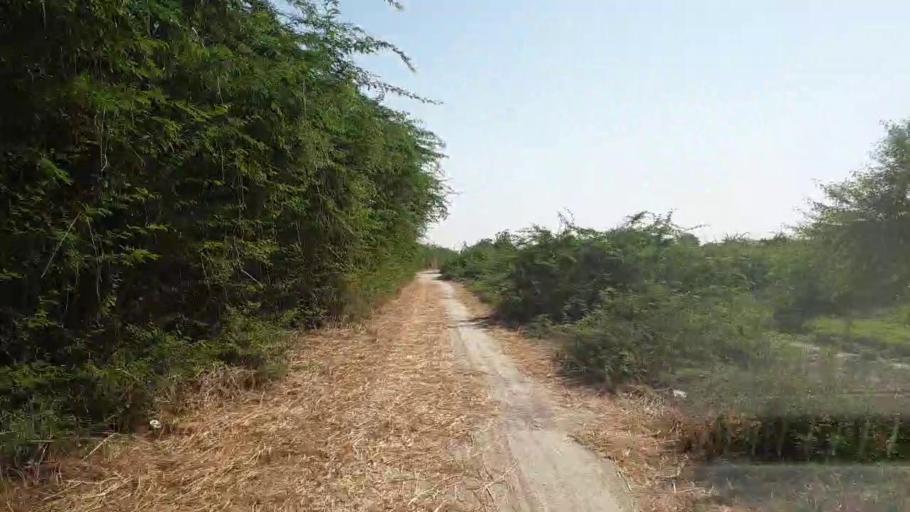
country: PK
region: Sindh
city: Tando Bago
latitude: 24.6359
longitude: 68.9921
